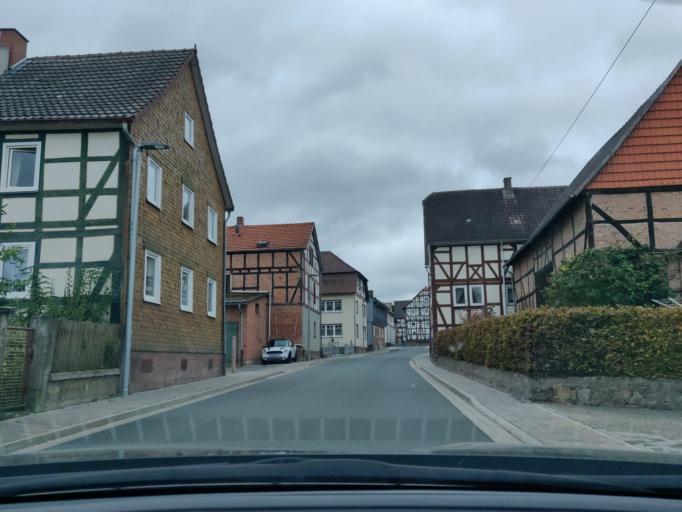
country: DE
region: Hesse
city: Fritzlar
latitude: 51.1794
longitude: 9.2680
